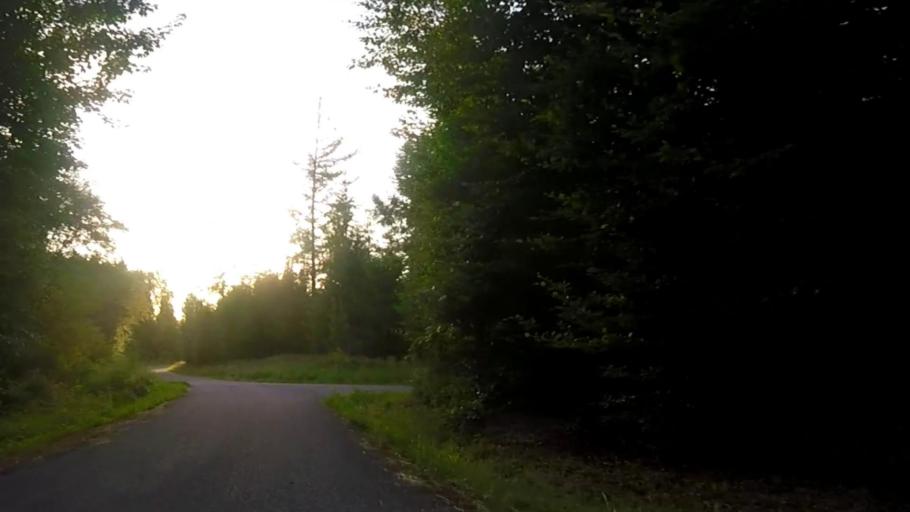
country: DE
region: Baden-Wuerttemberg
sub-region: Regierungsbezirk Stuttgart
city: Aspach
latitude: 49.0144
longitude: 9.4001
